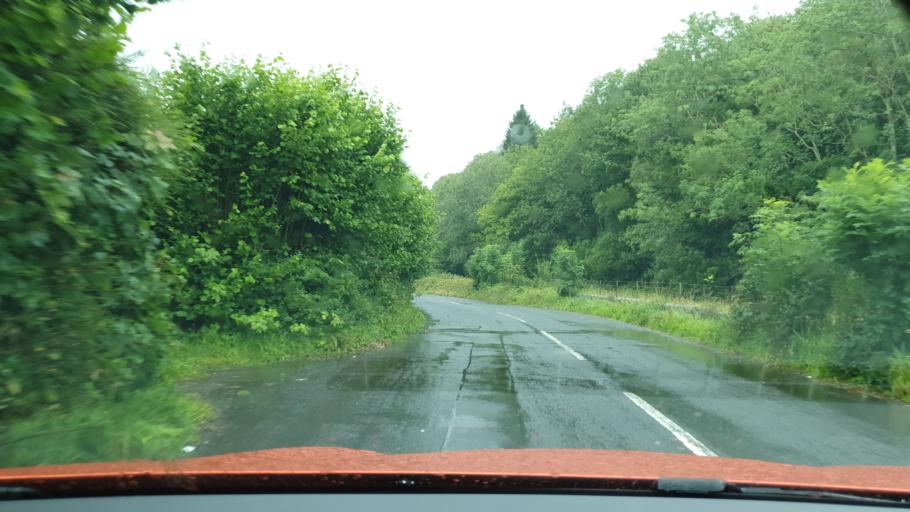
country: GB
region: England
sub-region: Cumbria
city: Millom
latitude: 54.2834
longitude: -3.2306
